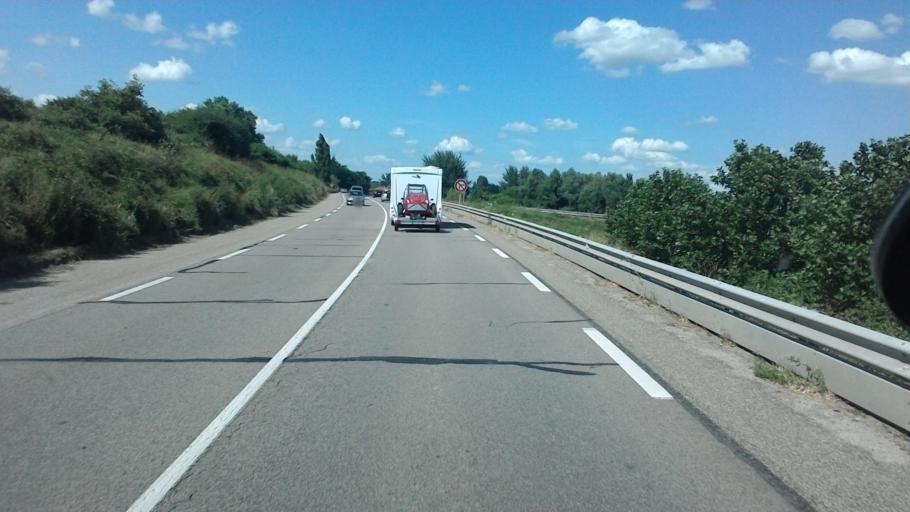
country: FR
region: Franche-Comte
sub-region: Departement du Jura
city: Tavaux
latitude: 47.0363
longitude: 5.4144
